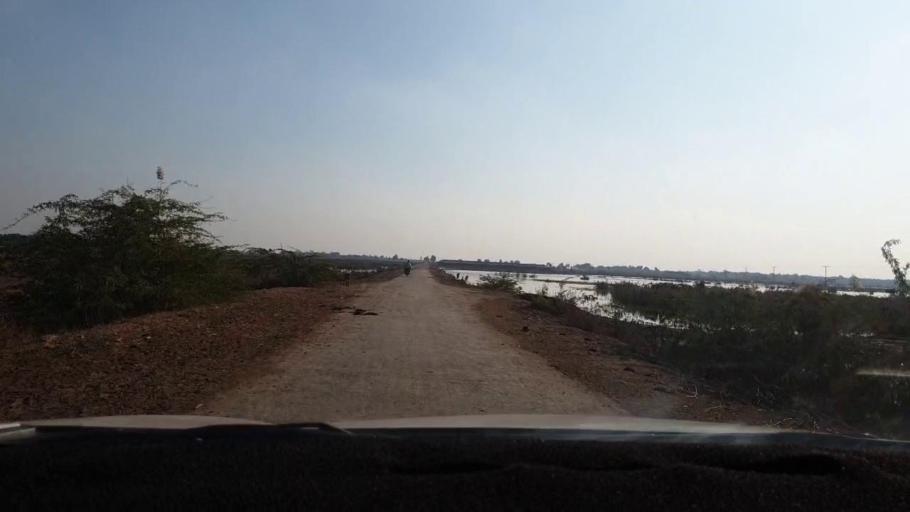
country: PK
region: Sindh
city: Berani
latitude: 25.7767
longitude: 68.7686
